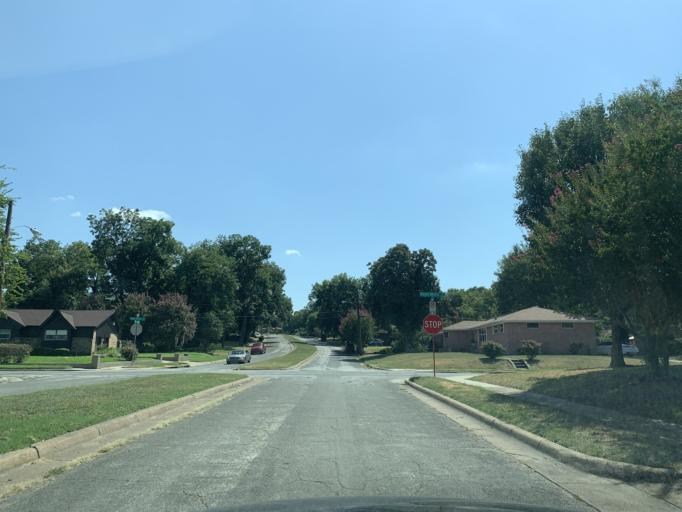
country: US
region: Texas
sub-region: Dallas County
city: Hutchins
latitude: 32.6791
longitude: -96.7962
